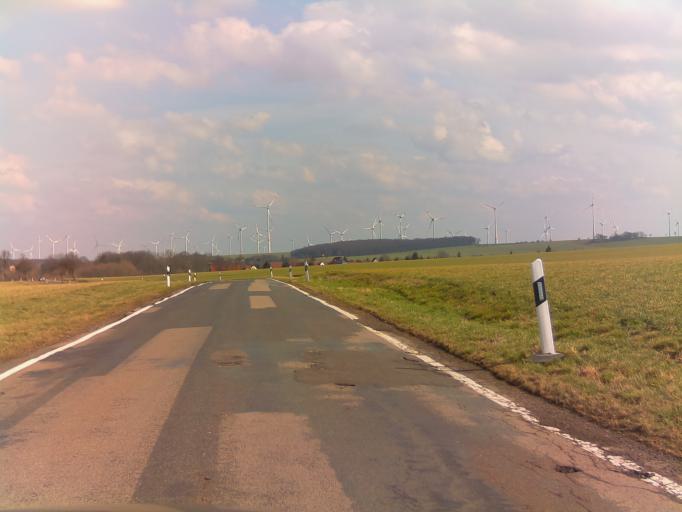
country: DE
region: Saxony-Anhalt
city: Leissling
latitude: 51.1560
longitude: 11.9036
